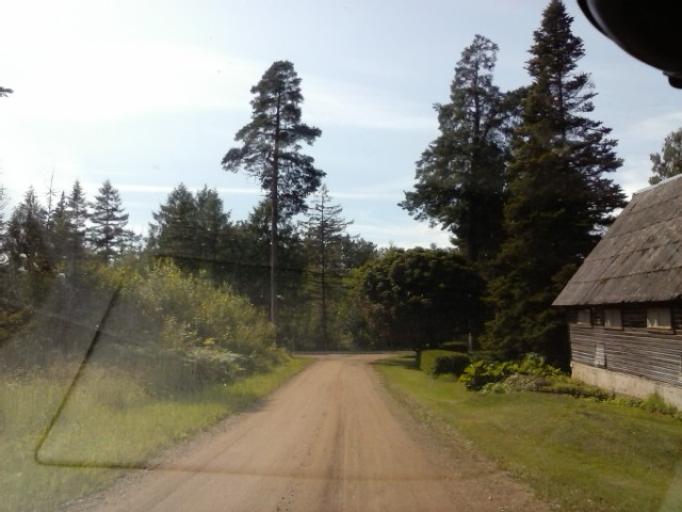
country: EE
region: Tartu
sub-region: UElenurme vald
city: Ulenurme
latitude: 58.2595
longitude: 26.9197
